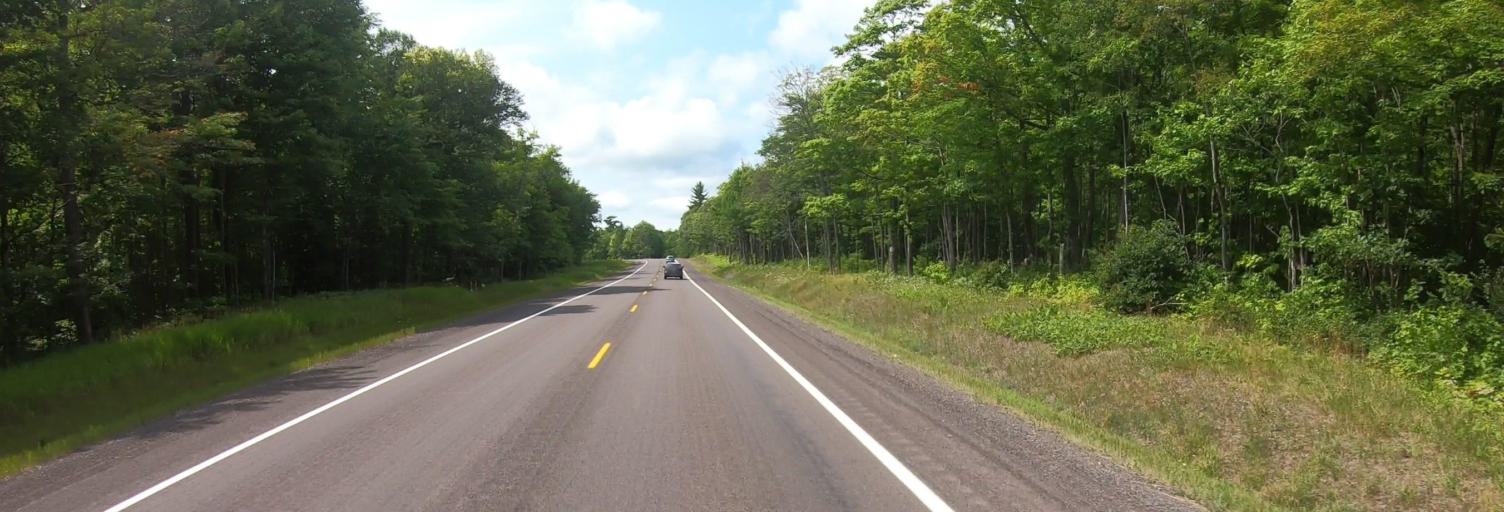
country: US
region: Michigan
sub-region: Houghton County
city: Hancock
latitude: 47.0302
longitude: -88.7088
